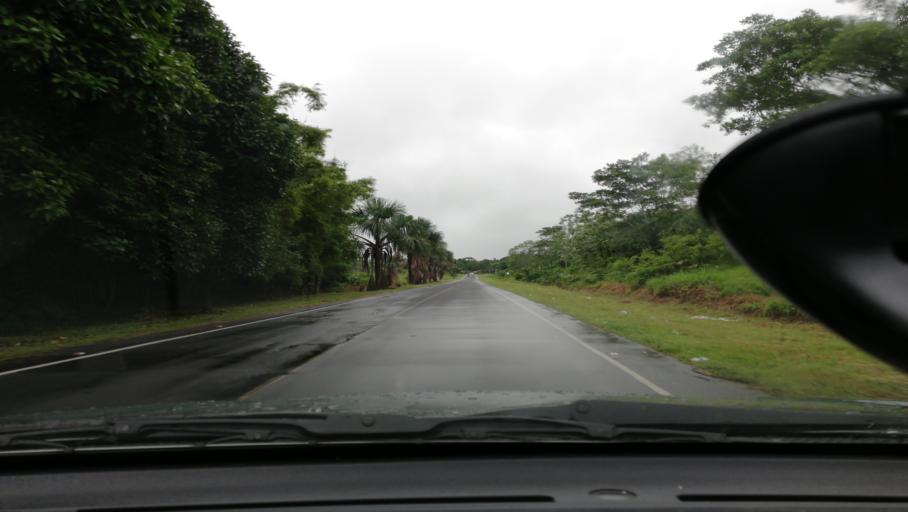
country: PE
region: Loreto
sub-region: Provincia de Maynas
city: San Juan
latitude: -4.0342
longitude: -73.4359
